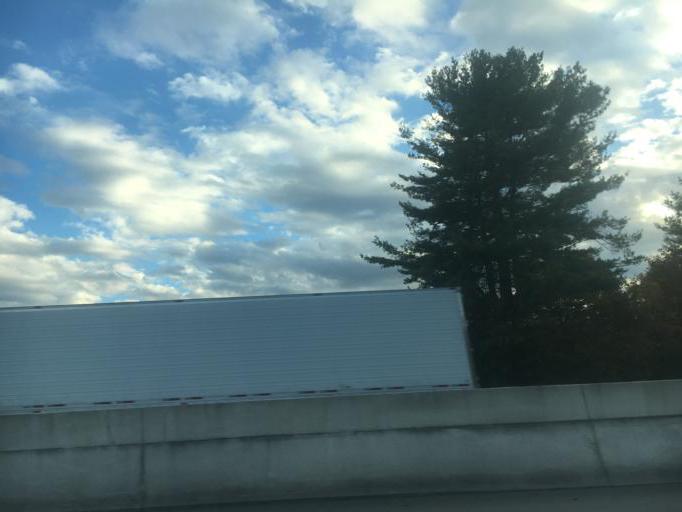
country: US
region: Tennessee
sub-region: Sullivan County
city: Fairmount
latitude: 36.6255
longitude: -82.1456
